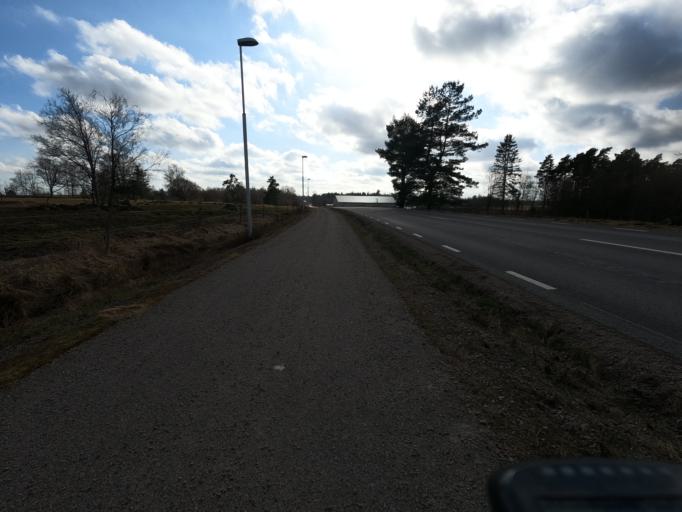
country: SE
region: Kronoberg
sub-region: Alvesta Kommun
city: Vislanda
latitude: 56.7457
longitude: 14.5544
